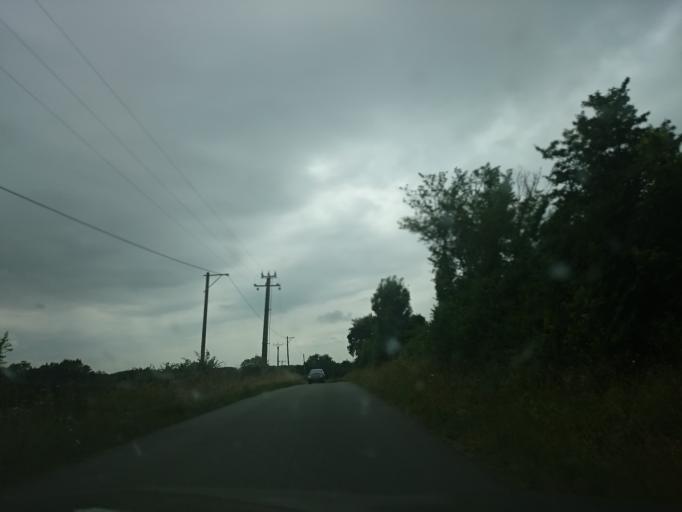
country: FR
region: Pays de la Loire
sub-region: Departement de la Loire-Atlantique
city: Le Pellerin
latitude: 47.2015
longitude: -1.7784
